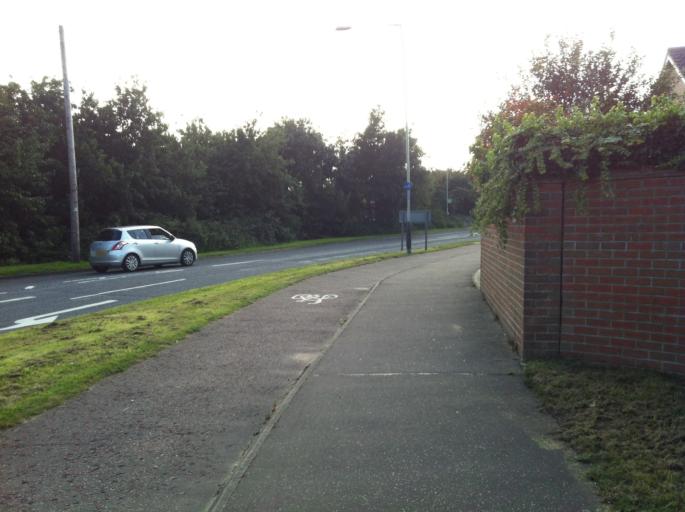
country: GB
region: England
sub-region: Norfolk
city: Bowthorpe
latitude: 52.6294
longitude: 1.2196
